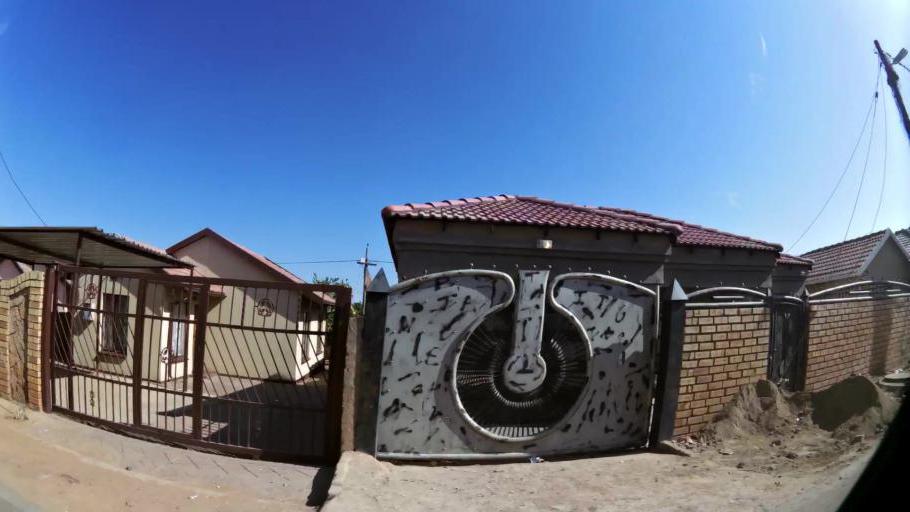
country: ZA
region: Gauteng
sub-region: City of Tshwane Metropolitan Municipality
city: Mabopane
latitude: -25.5564
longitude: 28.0732
